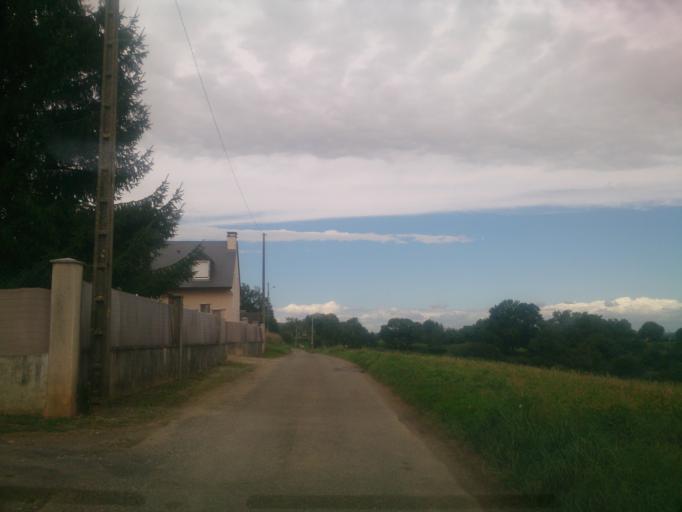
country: FR
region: Midi-Pyrenees
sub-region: Departement des Hautes-Pyrenees
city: Horgues
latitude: 43.1384
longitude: 0.0736
